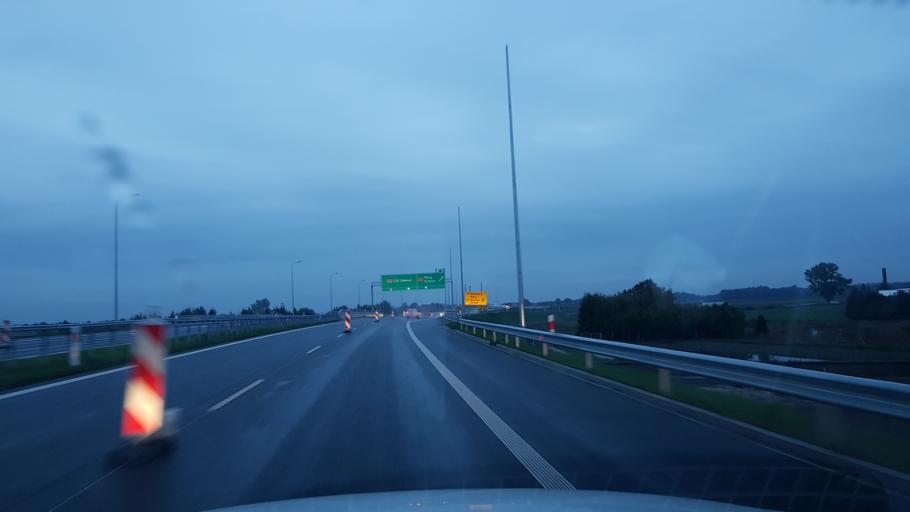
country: PL
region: West Pomeranian Voivodeship
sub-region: Powiat gryficki
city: Ploty
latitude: 53.8145
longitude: 15.2493
